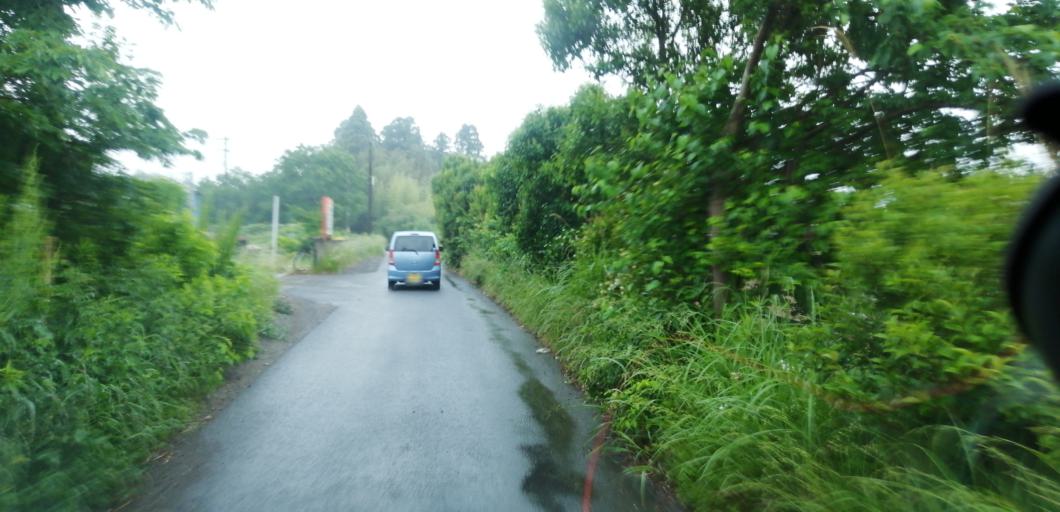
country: JP
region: Chiba
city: Ichihara
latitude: 35.4837
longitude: 140.1471
